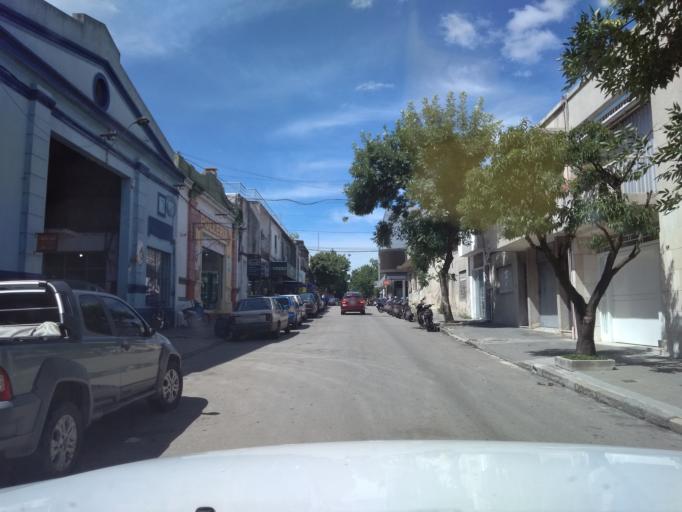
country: UY
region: Florida
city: Florida
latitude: -34.0988
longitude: -56.2161
